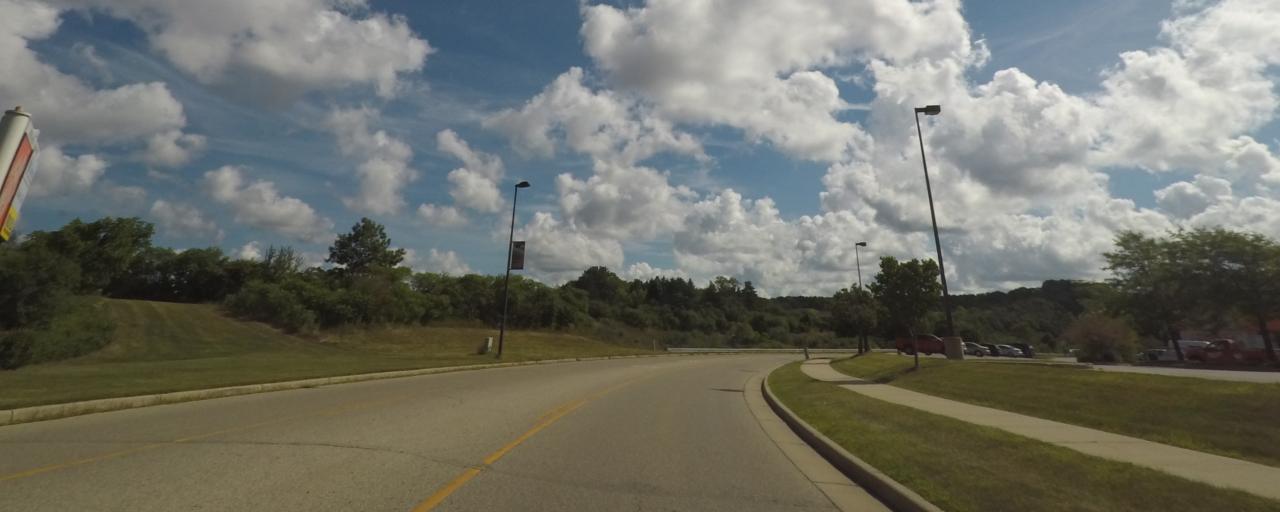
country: US
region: Wisconsin
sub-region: Waukesha County
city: Delafield
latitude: 43.0495
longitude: -88.3639
